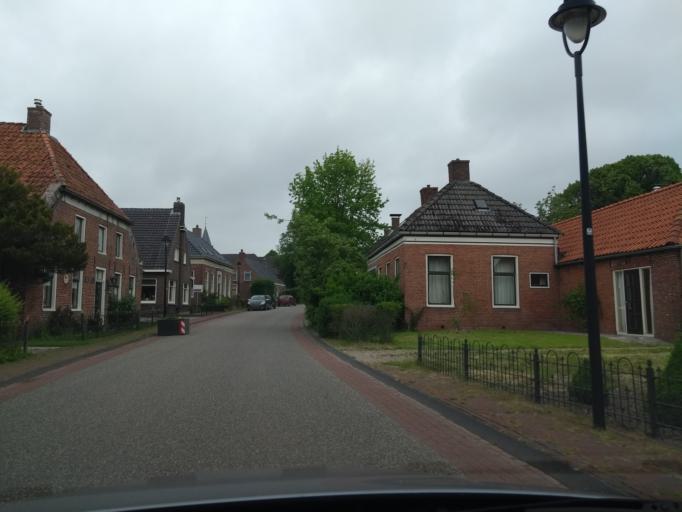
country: NL
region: Groningen
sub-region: Gemeente Zuidhorn
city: Oldehove
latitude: 53.3419
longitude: 6.4258
